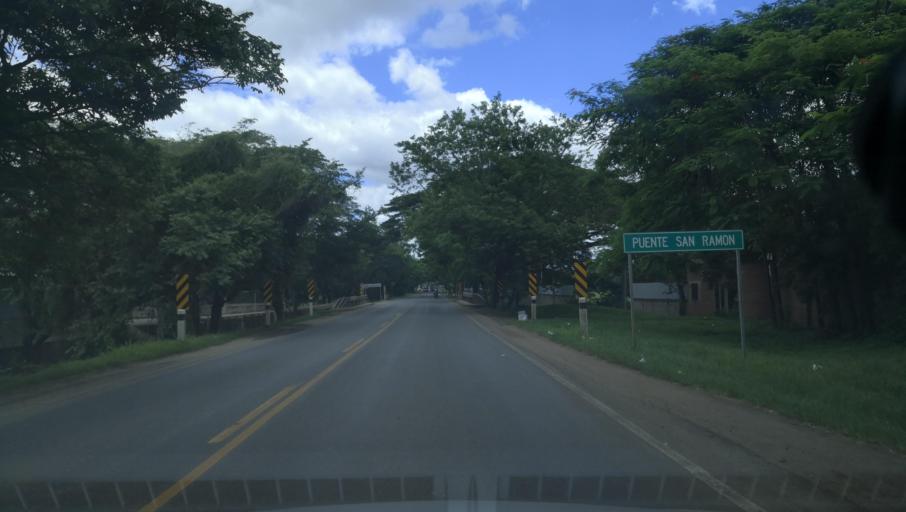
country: NI
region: Esteli
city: Esteli
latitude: 13.1174
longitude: -86.3620
